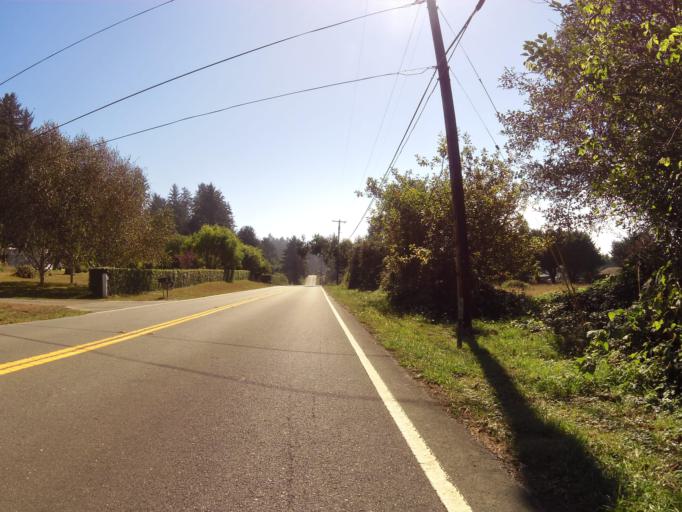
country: US
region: Oregon
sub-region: Curry County
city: Harbor
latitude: 41.9658
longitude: -124.1983
